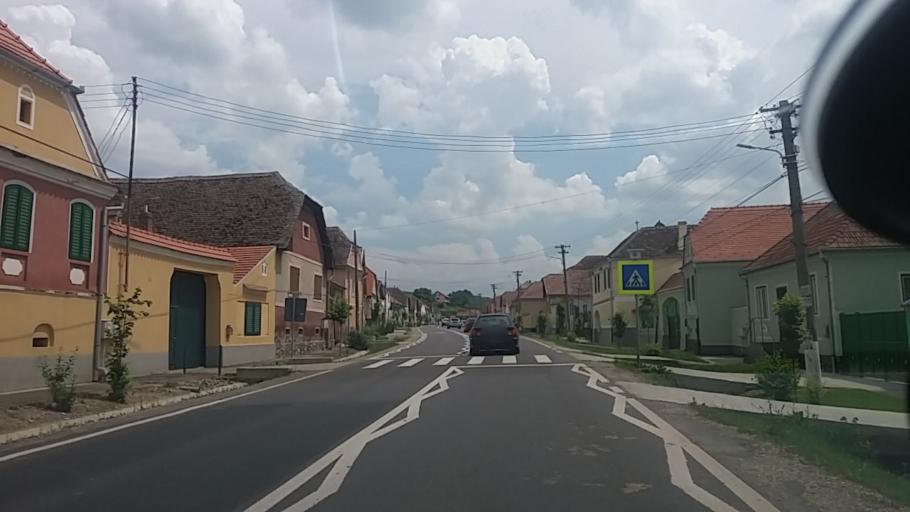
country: RO
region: Sibiu
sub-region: Comuna Slimnic
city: Slimnic
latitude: 45.9572
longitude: 24.1680
